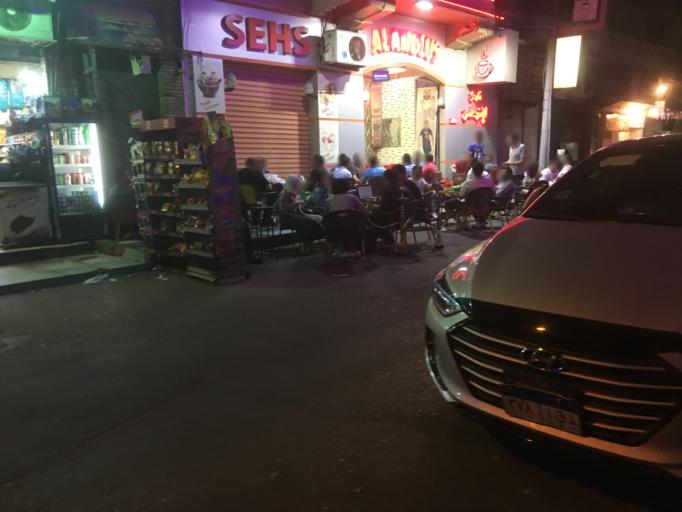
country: EG
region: Muhafazat al Qahirah
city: Cairo
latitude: 30.0957
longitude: 31.3355
